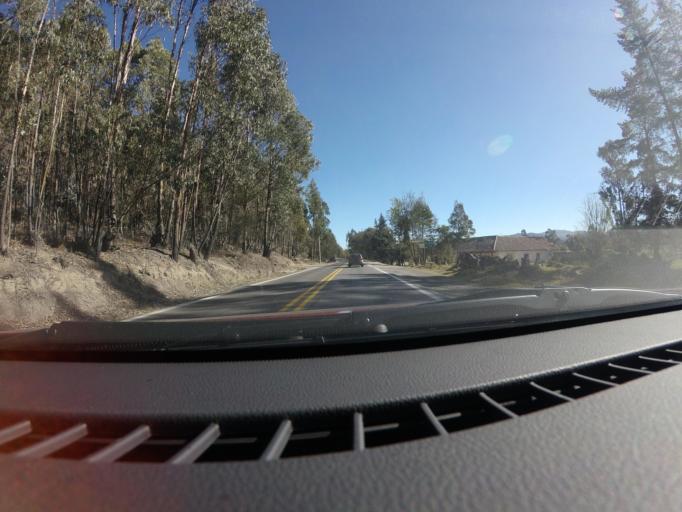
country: CO
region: Cundinamarca
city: Ubate
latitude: 5.2797
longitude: -73.8246
